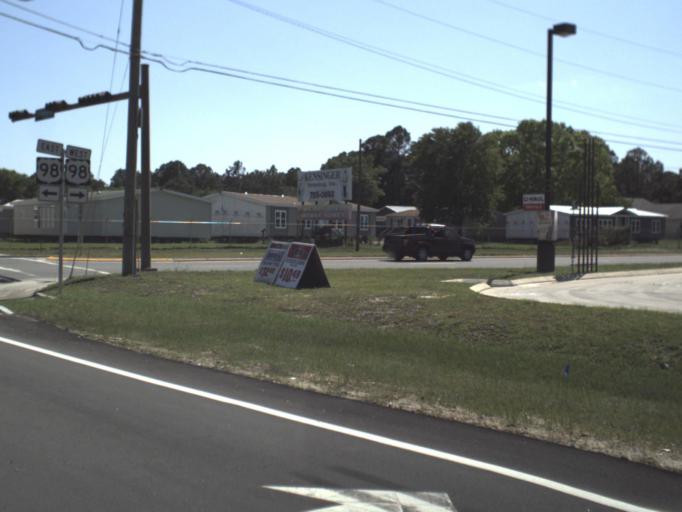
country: US
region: Florida
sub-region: Bay County
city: Cedar Grove
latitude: 30.1753
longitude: -85.6078
